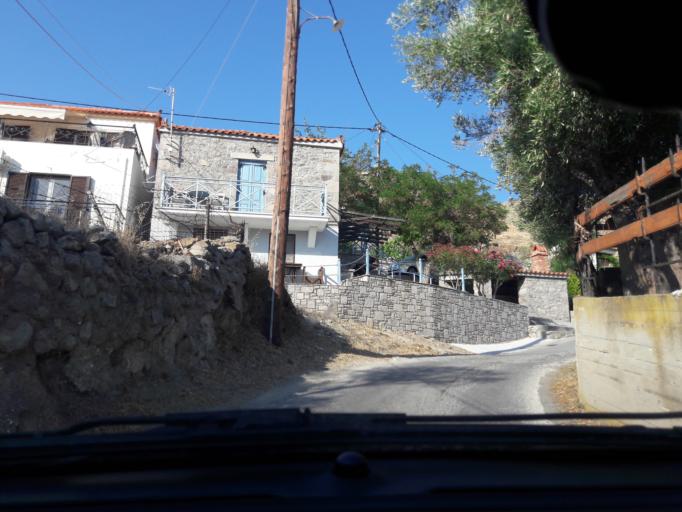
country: GR
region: North Aegean
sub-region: Nomos Lesvou
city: Myrina
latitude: 39.8531
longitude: 25.0888
